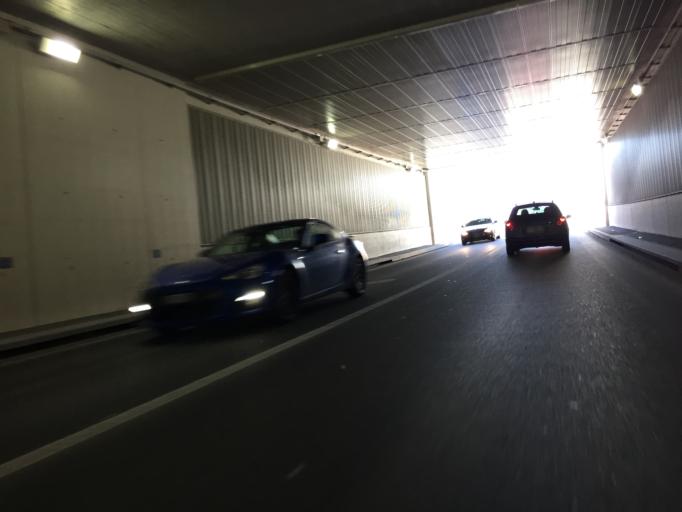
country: CH
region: Bern
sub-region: Bern-Mittelland District
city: Worb
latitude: 46.9313
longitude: 7.5572
